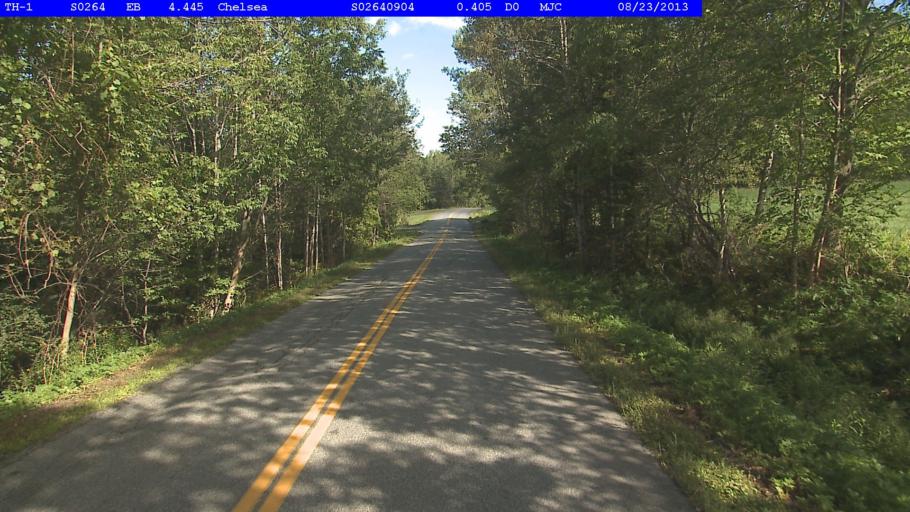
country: US
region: Vermont
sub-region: Orange County
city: Chelsea
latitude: 43.9730
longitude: -72.5044
